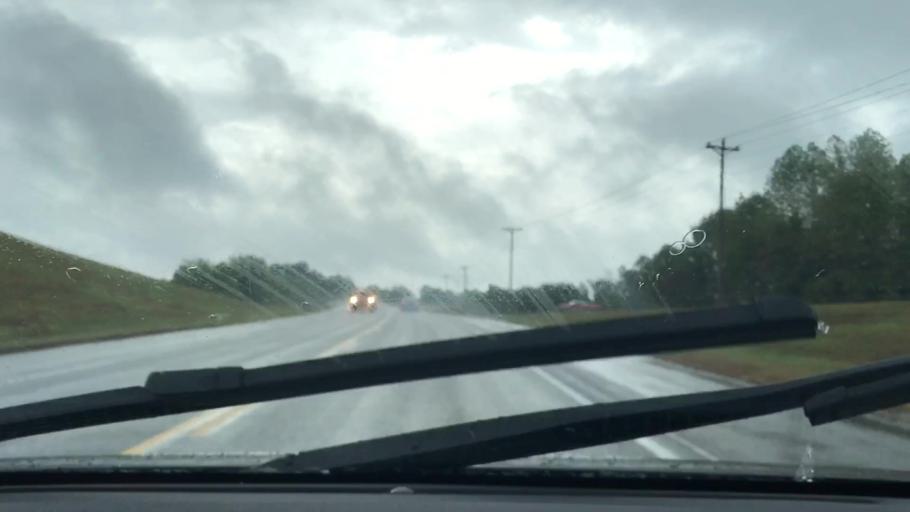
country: US
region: Tennessee
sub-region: Sumner County
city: Westmoreland
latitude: 36.5232
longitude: -86.1661
